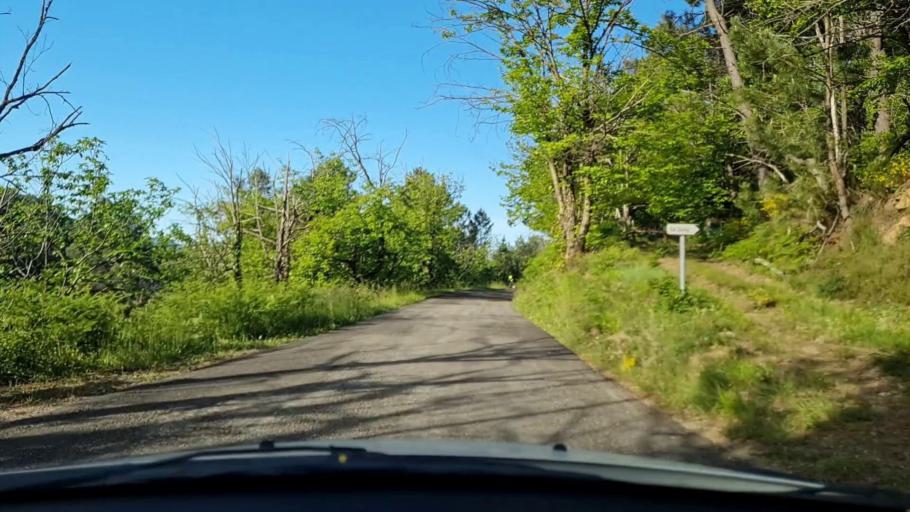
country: FR
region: Languedoc-Roussillon
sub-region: Departement du Gard
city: Branoux-les-Taillades
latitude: 44.1930
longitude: 3.9753
